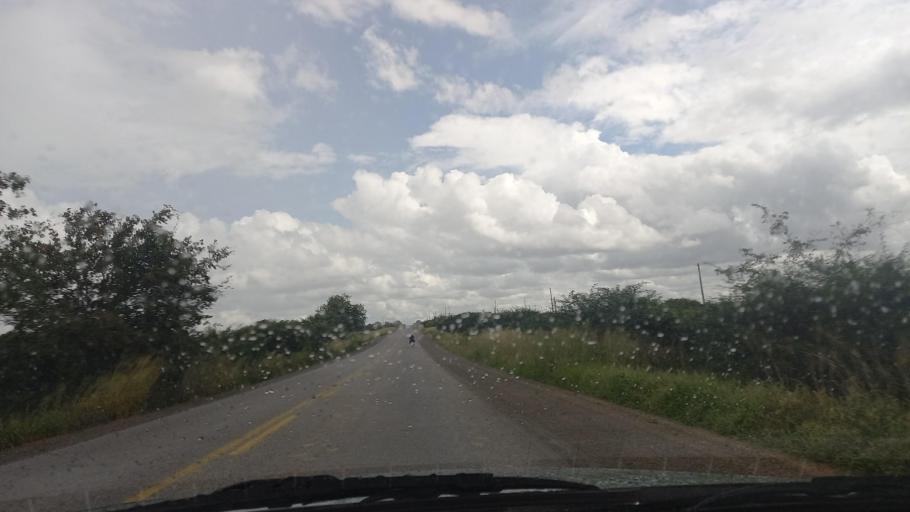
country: BR
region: Pernambuco
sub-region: Cachoeirinha
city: Cachoeirinha
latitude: -8.5630
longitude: -36.2775
